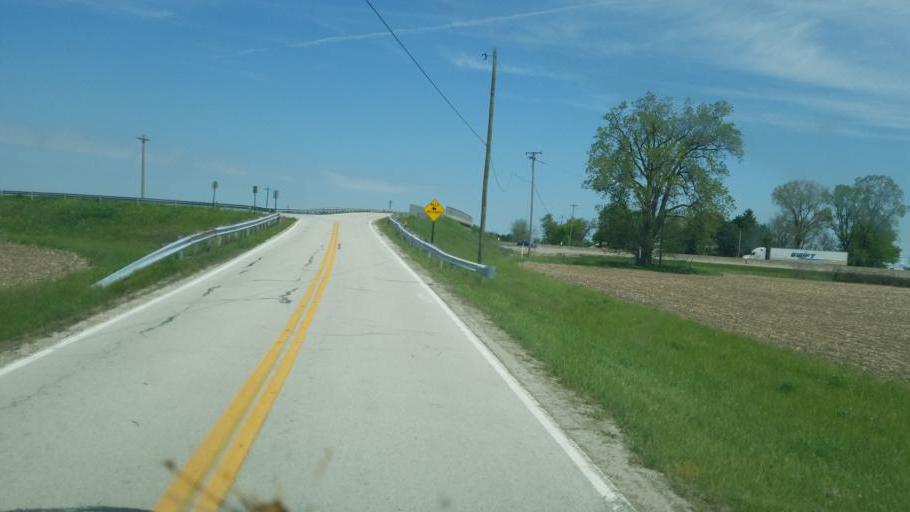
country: US
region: Ohio
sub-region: Sandusky County
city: Stony Prairie
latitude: 41.4283
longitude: -83.2015
